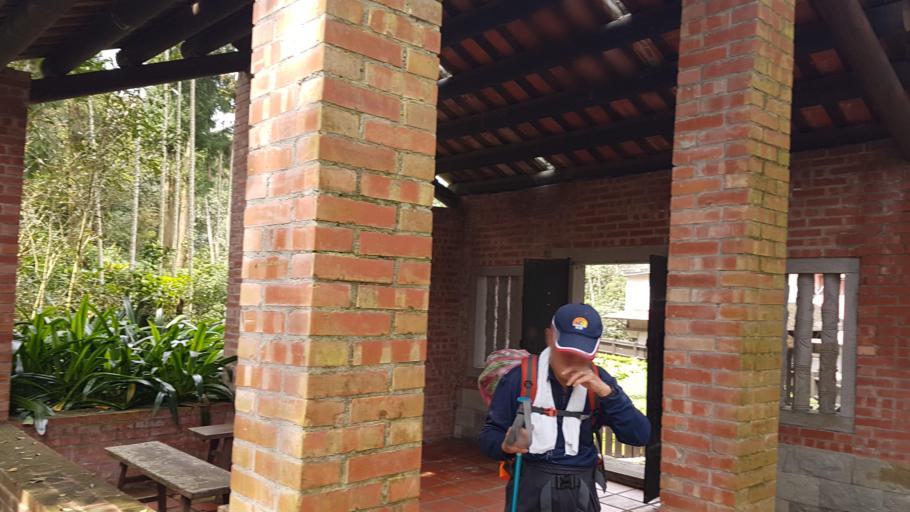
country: TW
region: Taipei
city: Taipei
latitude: 24.9696
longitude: 121.5809
